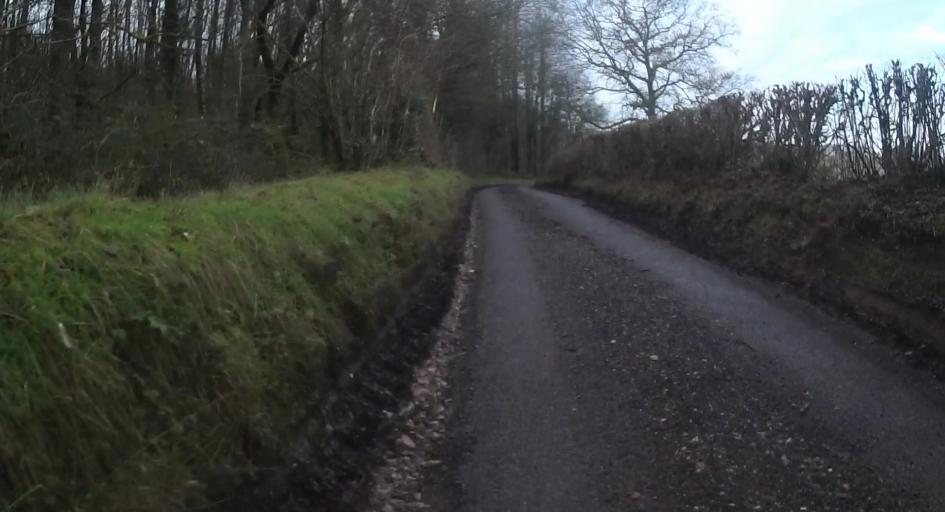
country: GB
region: England
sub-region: Hampshire
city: Kingsclere
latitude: 51.2905
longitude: -1.1982
